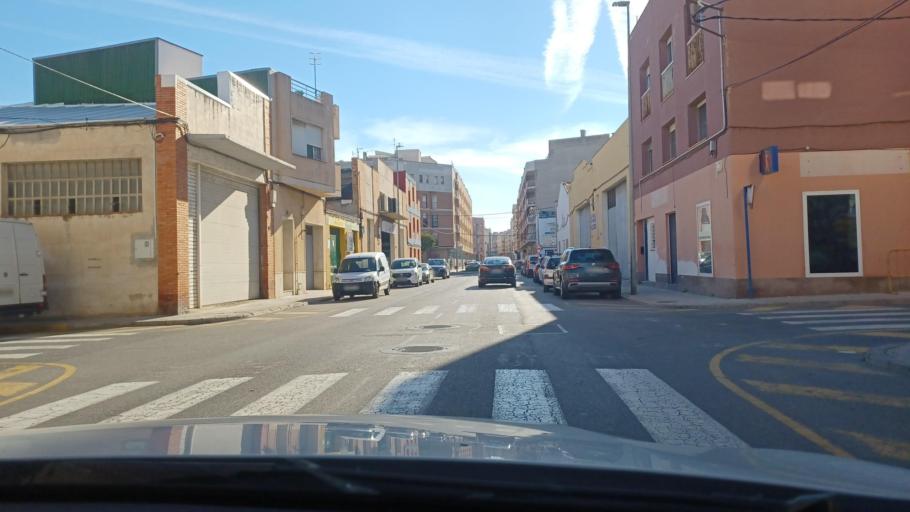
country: ES
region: Catalonia
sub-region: Provincia de Tarragona
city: Amposta
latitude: 40.7068
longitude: 0.5806
